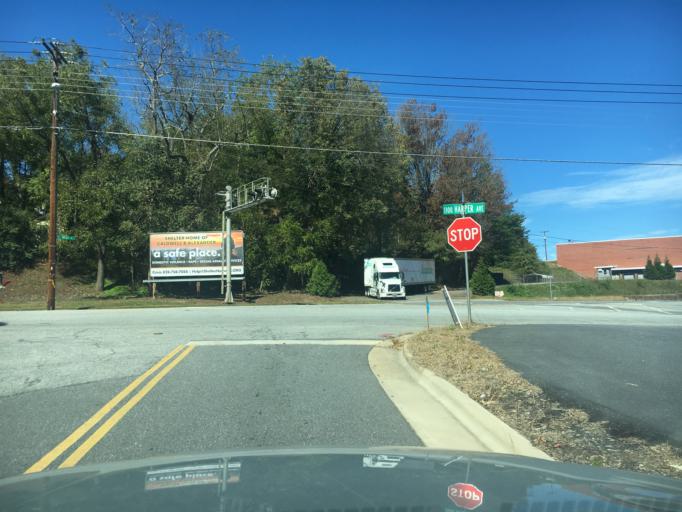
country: US
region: North Carolina
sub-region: Caldwell County
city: Lenoir
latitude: 35.9109
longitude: -81.5456
